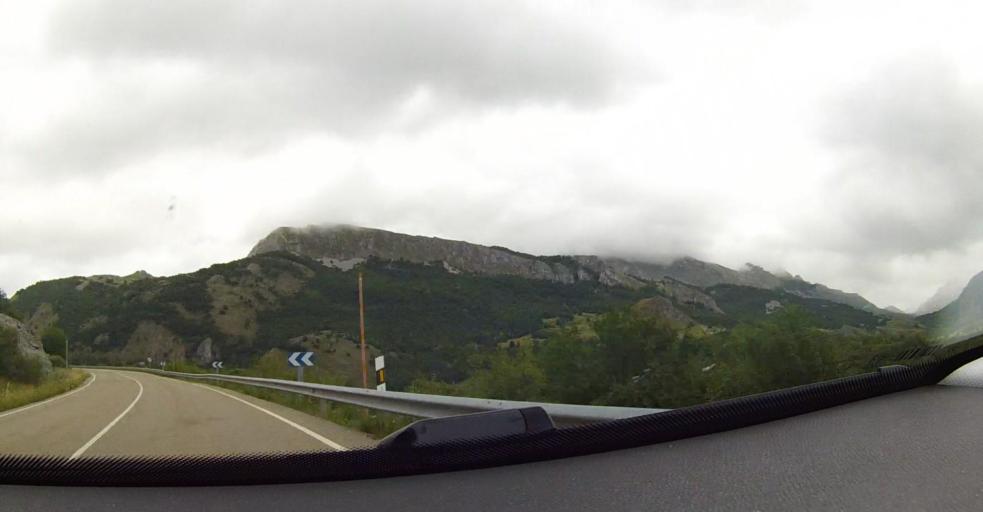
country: ES
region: Castille and Leon
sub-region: Provincia de Leon
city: Buron
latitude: 43.0203
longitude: -5.0360
